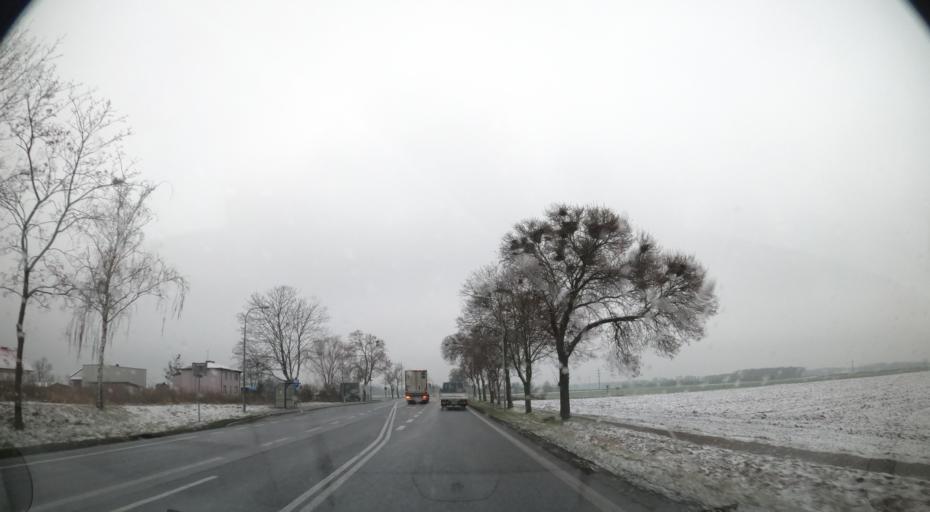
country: PL
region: Masovian Voivodeship
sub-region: Powiat sochaczewski
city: Teresin
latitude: 52.2158
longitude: 20.3879
